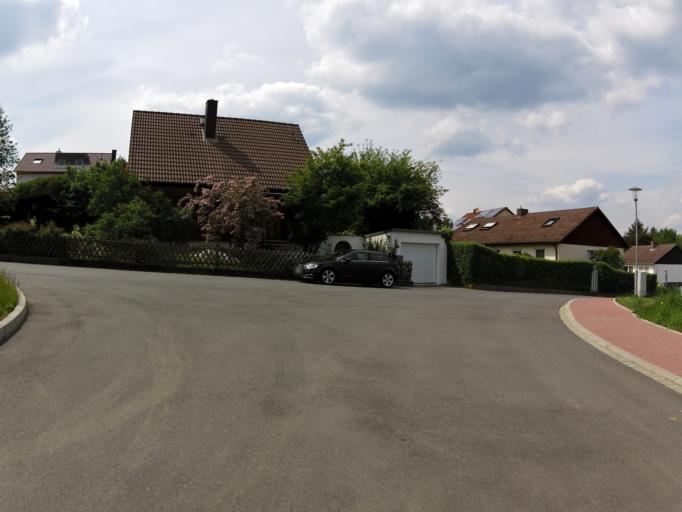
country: DE
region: Bavaria
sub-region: Regierungsbezirk Unterfranken
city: Reichenberg
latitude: 49.7307
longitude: 9.9117
